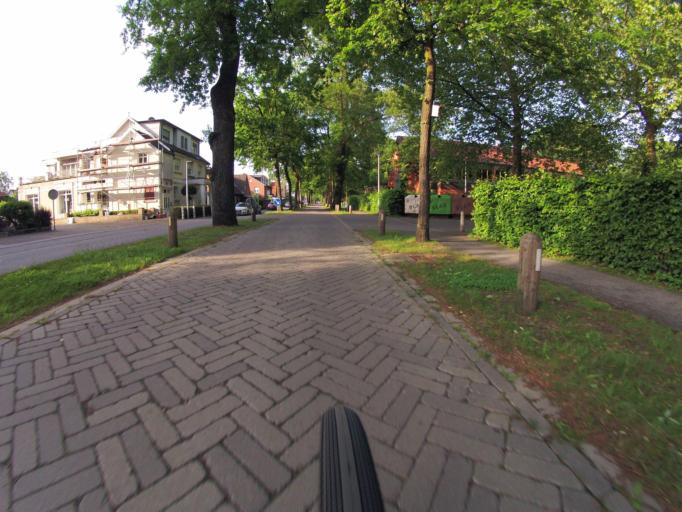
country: DE
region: North Rhine-Westphalia
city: Ibbenburen
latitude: 52.2686
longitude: 7.7093
